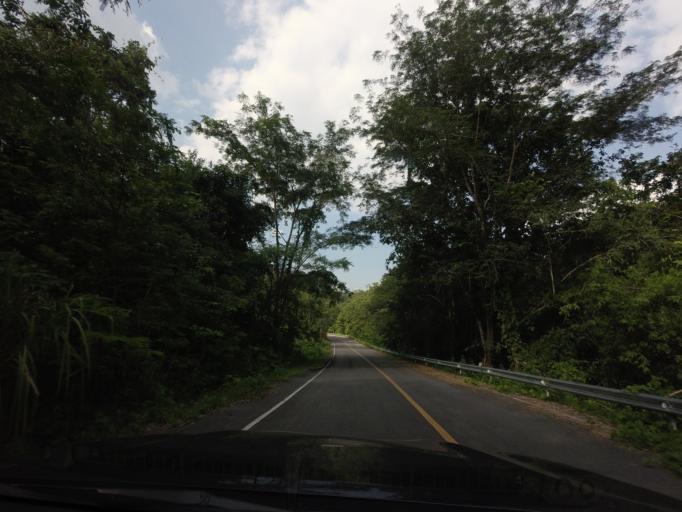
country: TH
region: Nan
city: Na Noi
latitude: 18.3065
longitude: 100.9060
